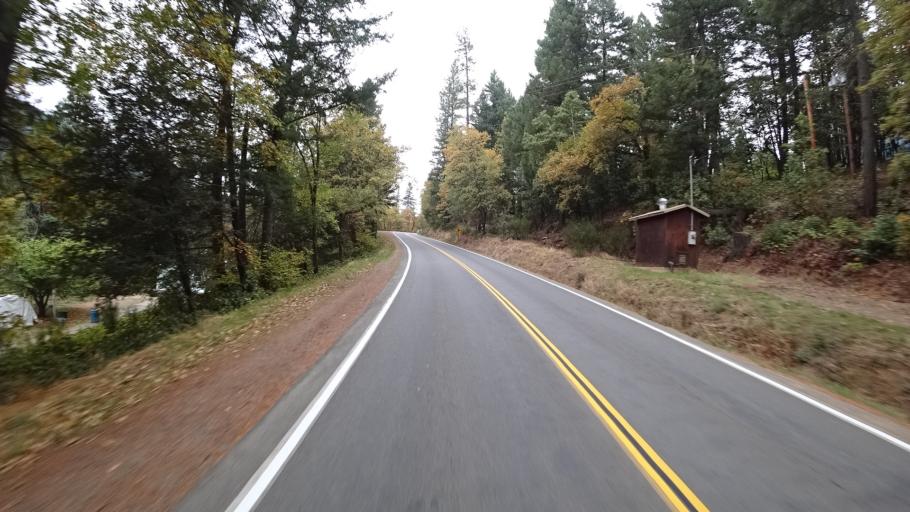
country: US
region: California
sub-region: Siskiyou County
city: Happy Camp
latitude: 41.8008
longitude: -123.3776
